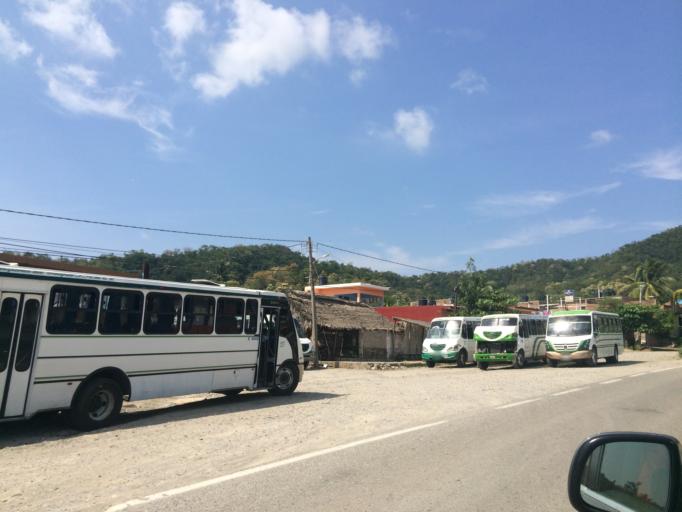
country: MX
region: Jalisco
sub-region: Cihuatlan
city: Emiliano Zapata (El Ranchito)
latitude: 19.2434
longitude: -104.7169
